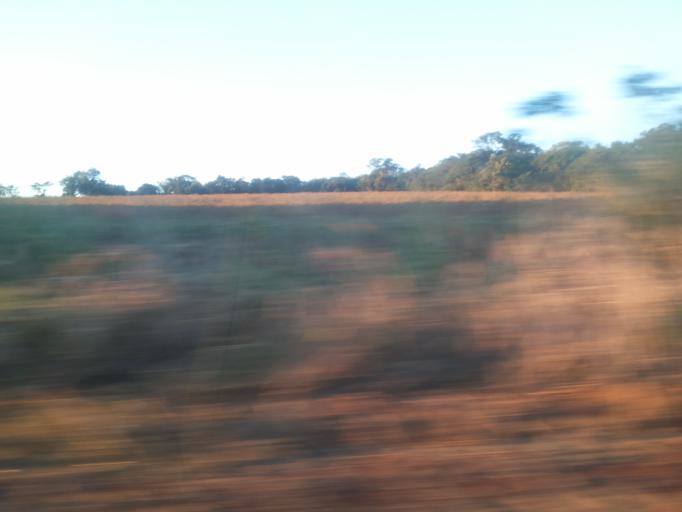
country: BR
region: Minas Gerais
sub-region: Capinopolis
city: Capinopolis
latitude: -18.6776
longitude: -49.5585
